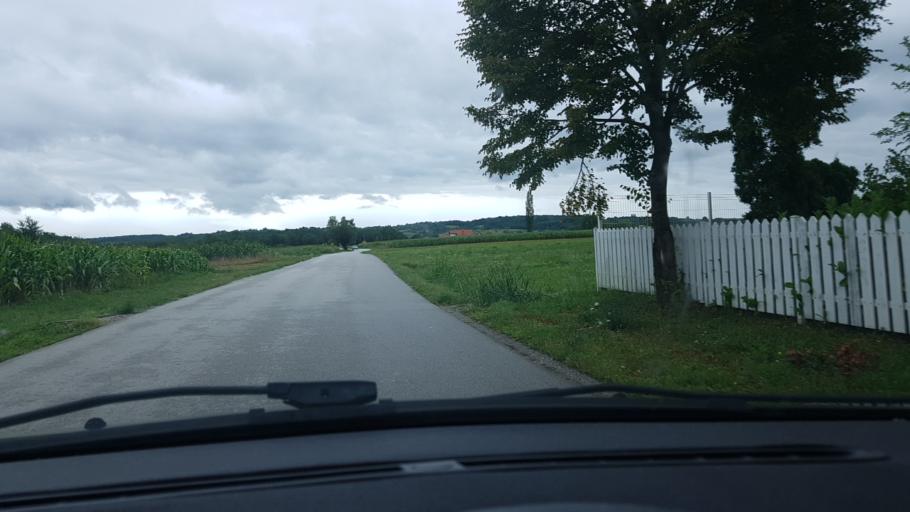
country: HR
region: Karlovacka
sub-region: Grad Karlovac
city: Karlovac
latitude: 45.5558
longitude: 15.5402
